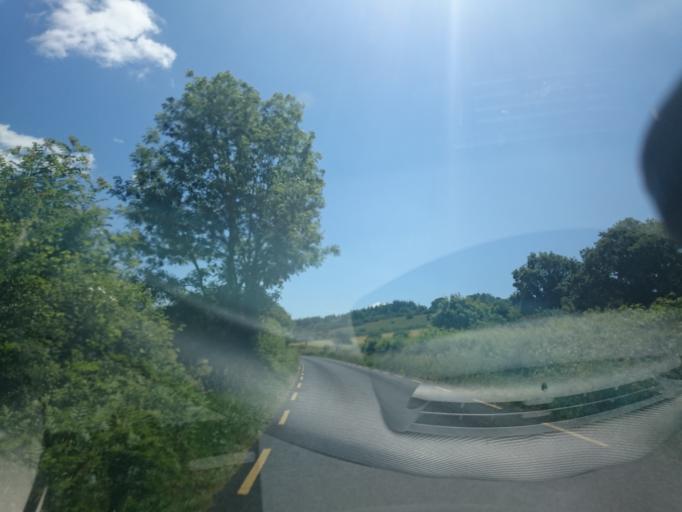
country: IE
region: Leinster
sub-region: Kilkenny
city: Graiguenamanagh
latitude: 52.5856
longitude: -6.9582
